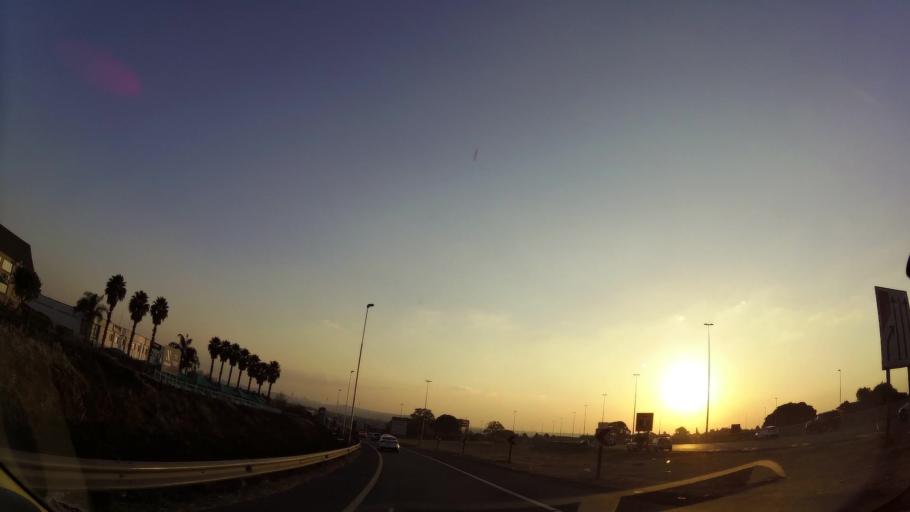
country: ZA
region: Gauteng
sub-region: Ekurhuleni Metropolitan Municipality
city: Germiston
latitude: -26.1639
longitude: 28.1705
